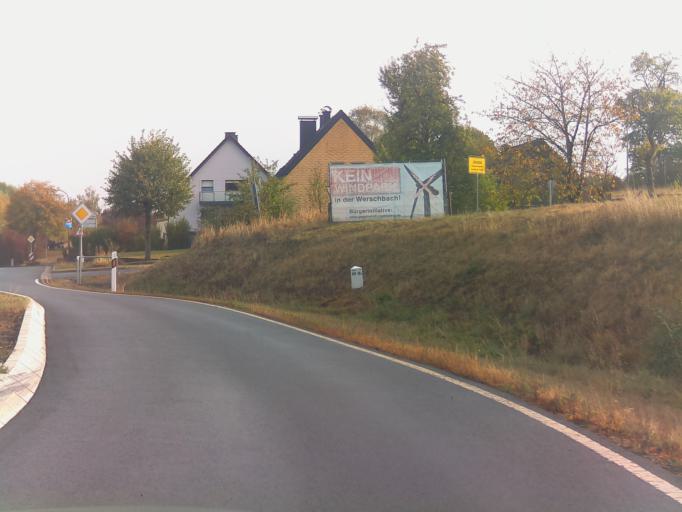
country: DE
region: Hesse
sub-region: Regierungsbezirk Kassel
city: Hosenfeld
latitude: 50.4867
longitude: 9.4498
